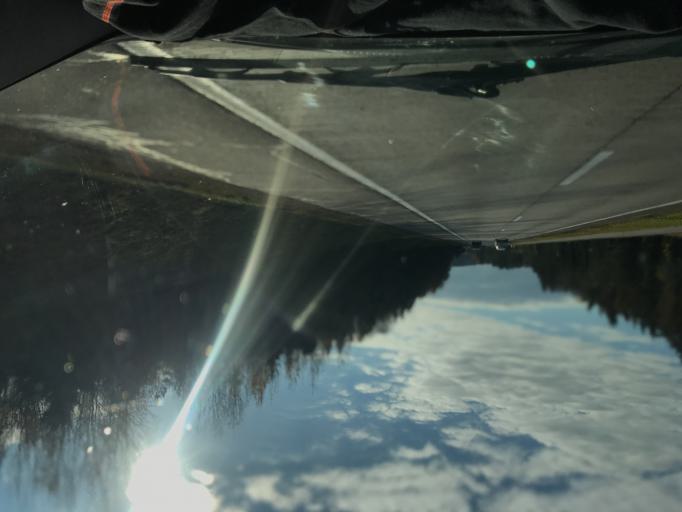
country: BY
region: Minsk
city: Lahoysk
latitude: 54.1253
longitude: 27.8074
